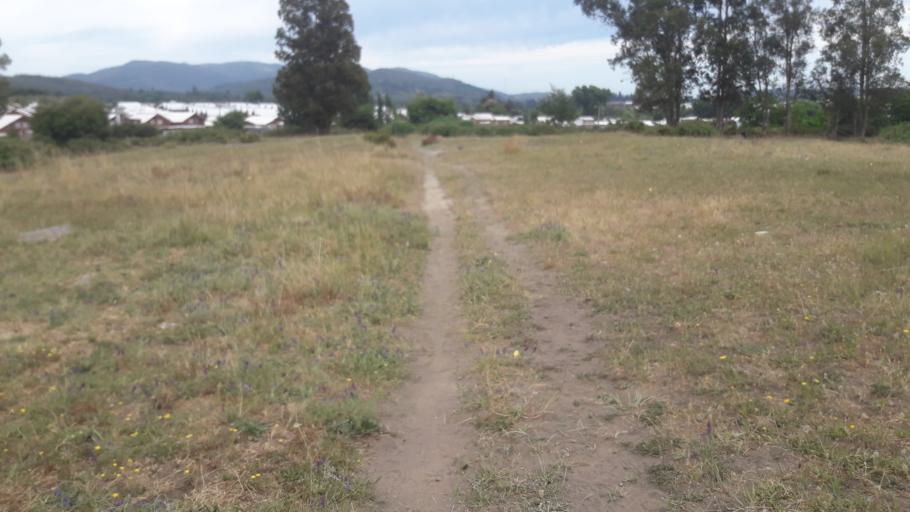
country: CL
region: Biobio
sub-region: Provincia de Biobio
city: Nacimiento
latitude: -37.5034
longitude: -72.6880
